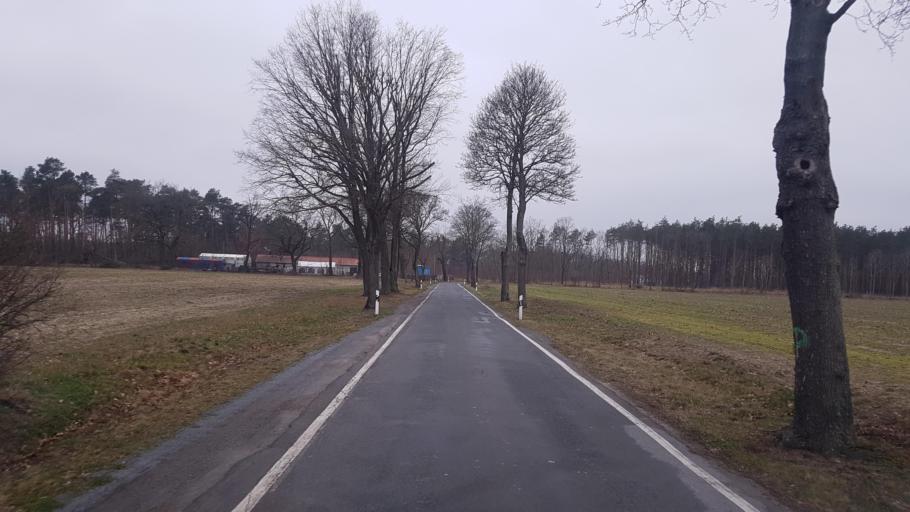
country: DE
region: Brandenburg
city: Herzberg
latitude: 51.6817
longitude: 13.1946
